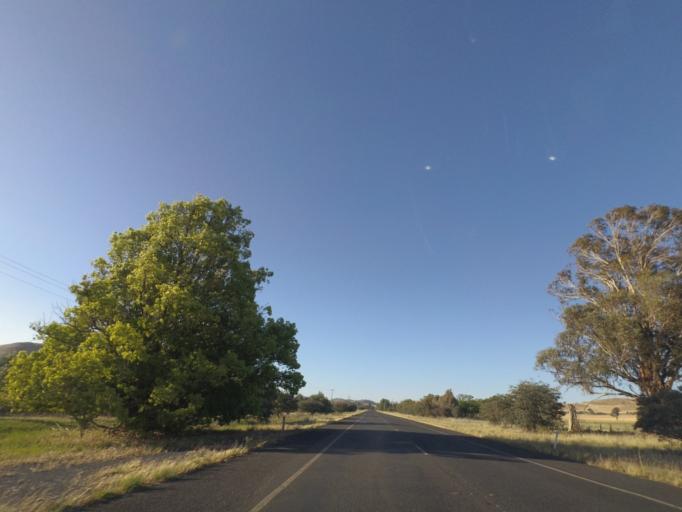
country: AU
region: New South Wales
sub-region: Gundagai
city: Gundagai
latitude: -34.9419
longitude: 148.1683
